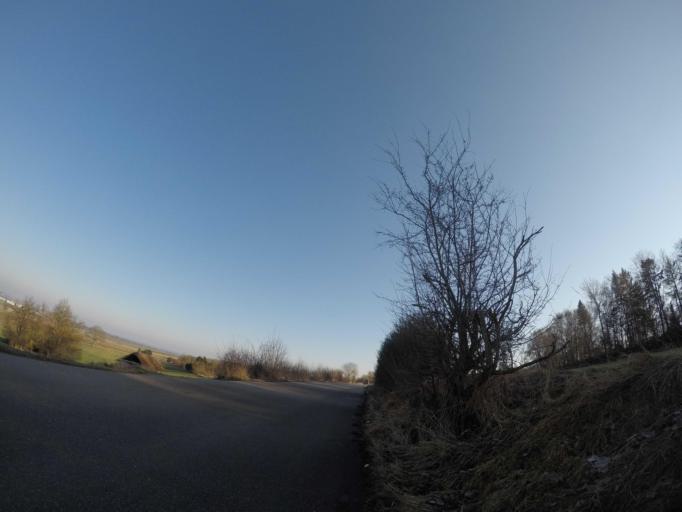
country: DE
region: Baden-Wuerttemberg
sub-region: Tuebingen Region
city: Bernstadt
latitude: 48.4813
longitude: 10.0638
